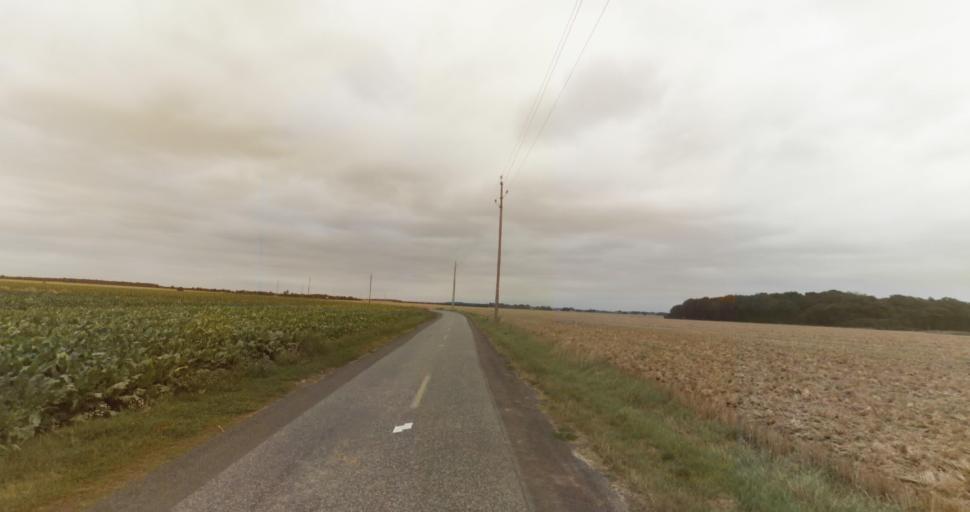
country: FR
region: Haute-Normandie
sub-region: Departement de l'Eure
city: Marcilly-sur-Eure
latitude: 48.9185
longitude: 1.3045
